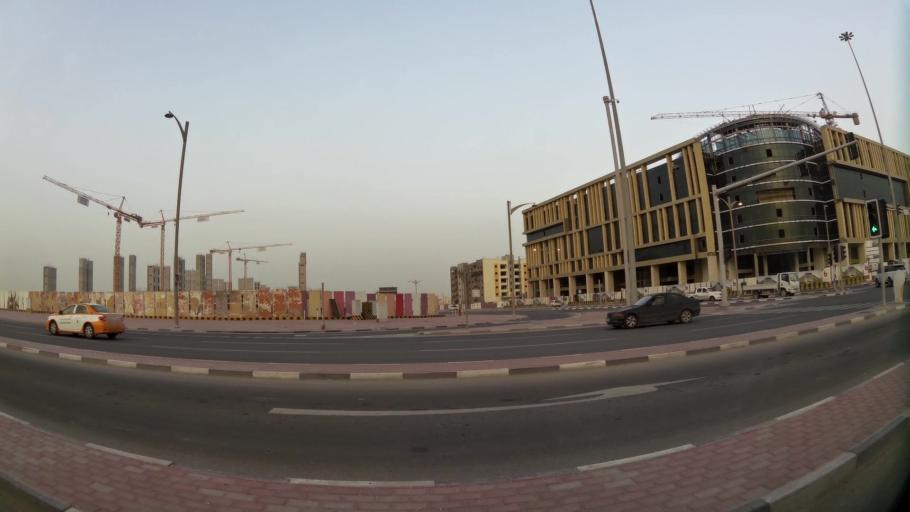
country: QA
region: Baladiyat ad Dawhah
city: Doha
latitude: 25.2534
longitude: 51.4697
